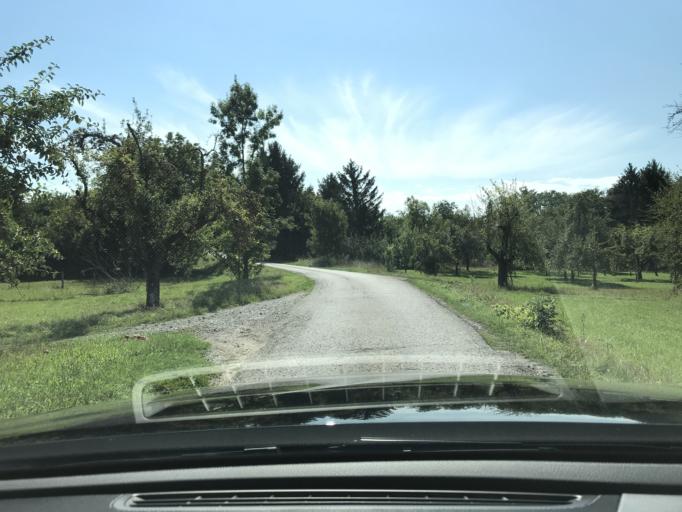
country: DE
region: Baden-Wuerttemberg
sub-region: Regierungsbezirk Stuttgart
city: Affalterbach
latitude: 48.8978
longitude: 9.3127
